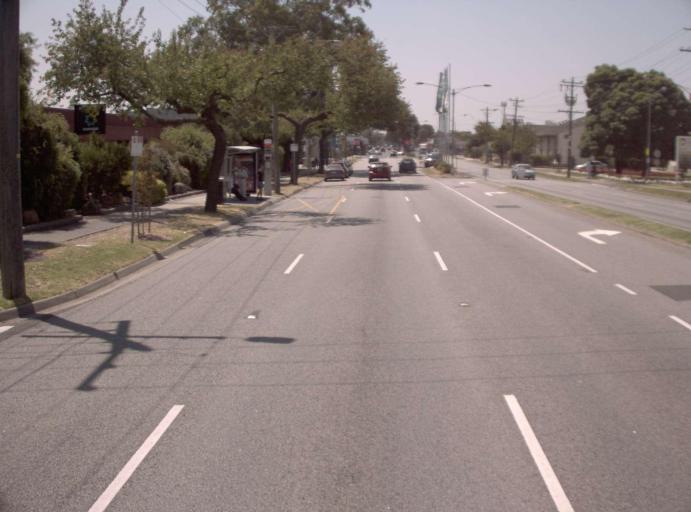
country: AU
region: Victoria
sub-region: Greater Dandenong
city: Springvale
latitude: -37.9566
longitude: 145.1514
